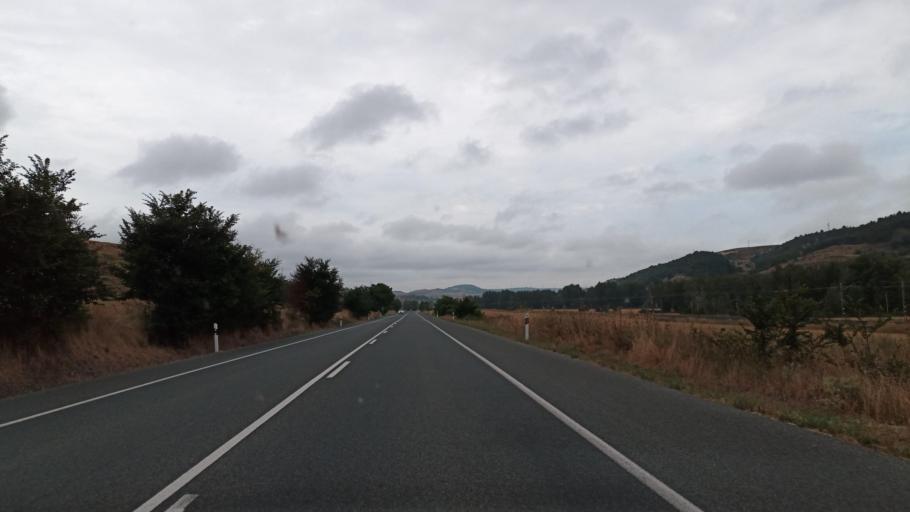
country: ES
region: Castille and Leon
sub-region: Provincia de Burgos
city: Pradanos de Bureba
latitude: 42.5173
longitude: -3.3365
